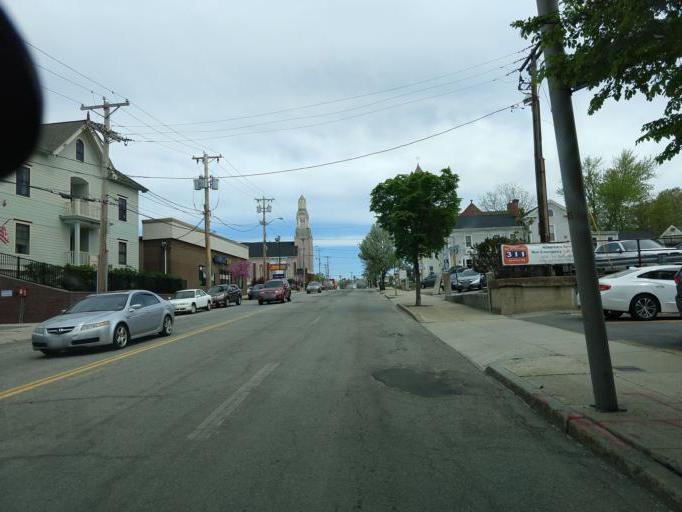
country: US
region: Massachusetts
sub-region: Essex County
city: Haverhill
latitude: 42.7783
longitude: -71.0773
